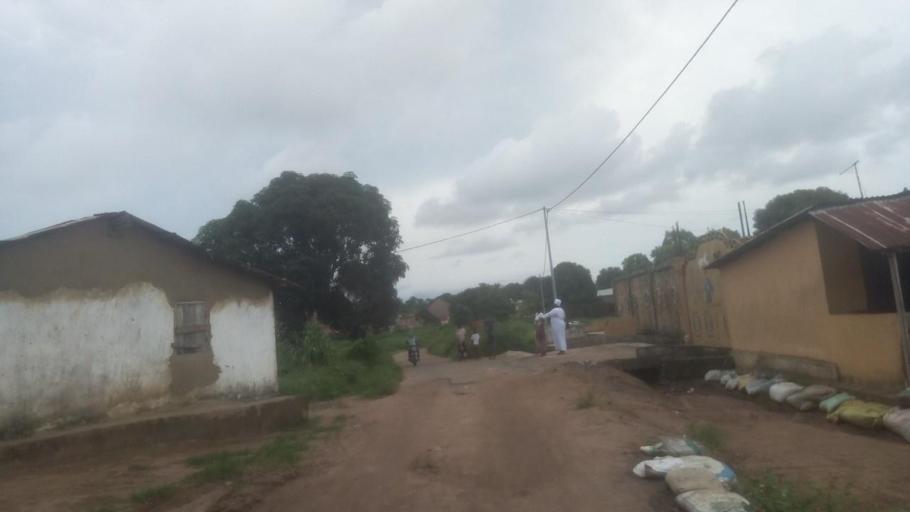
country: SL
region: Northern Province
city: Masoyila
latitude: 8.6079
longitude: -13.1908
